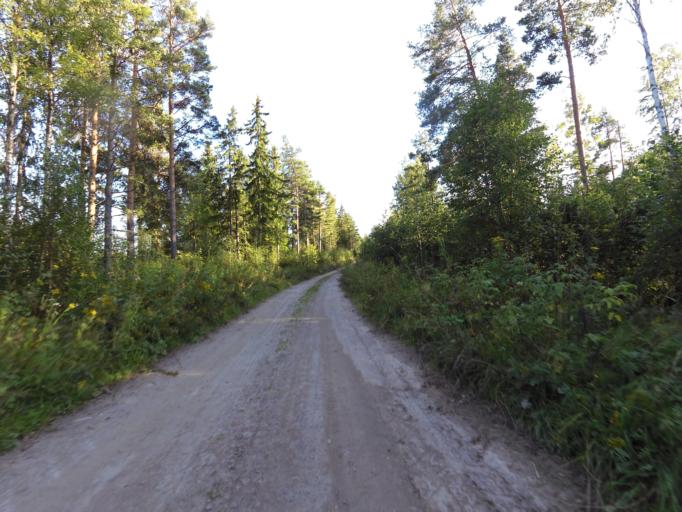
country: SE
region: Gaevleborg
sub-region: Gavle Kommun
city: Gavle
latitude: 60.6510
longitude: 17.1158
